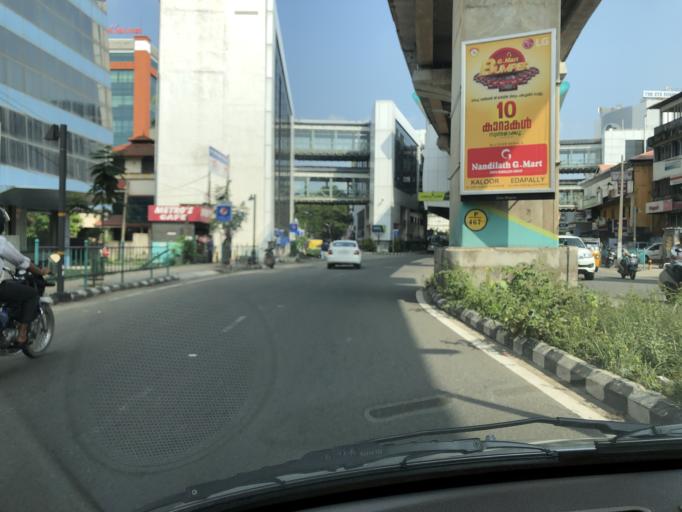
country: IN
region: Kerala
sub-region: Ernakulam
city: Elur
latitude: 10.0141
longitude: 76.3023
